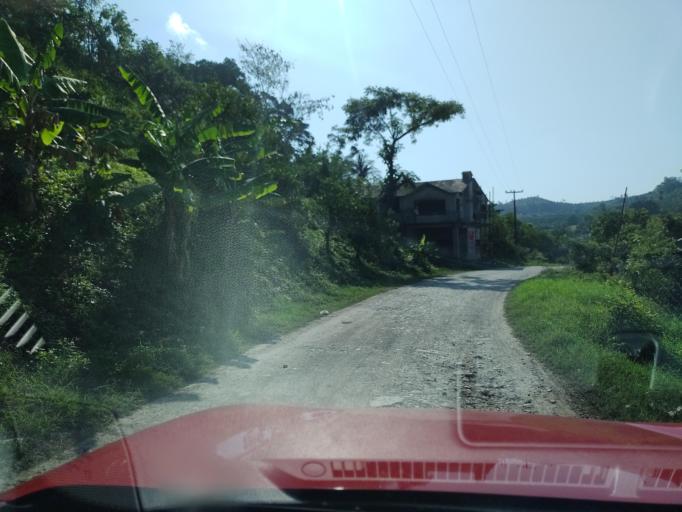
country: MX
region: Veracruz
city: Agua Dulce
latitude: 20.2908
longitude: -97.1831
